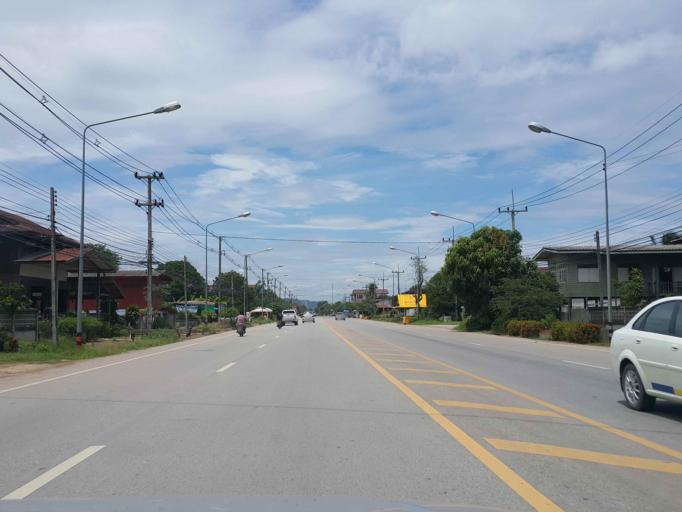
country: TH
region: Sukhothai
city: Ban Na
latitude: 17.0134
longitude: 99.7610
